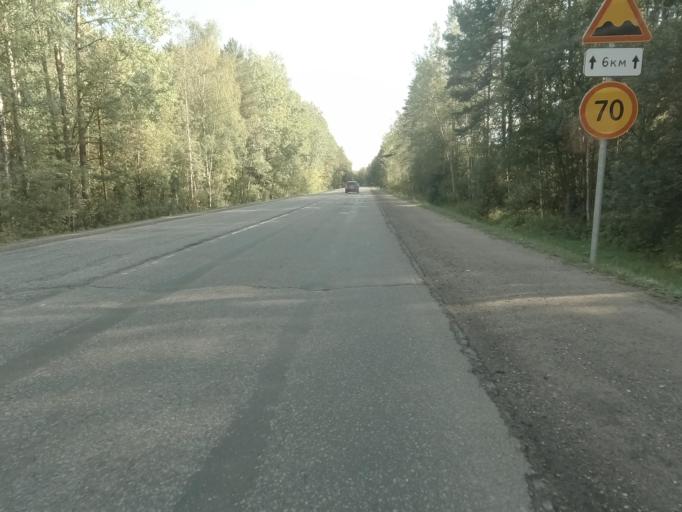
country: RU
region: Leningrad
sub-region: Volosovskiy Rayon
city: Shlissel'burg
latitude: 59.9445
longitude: 30.9845
